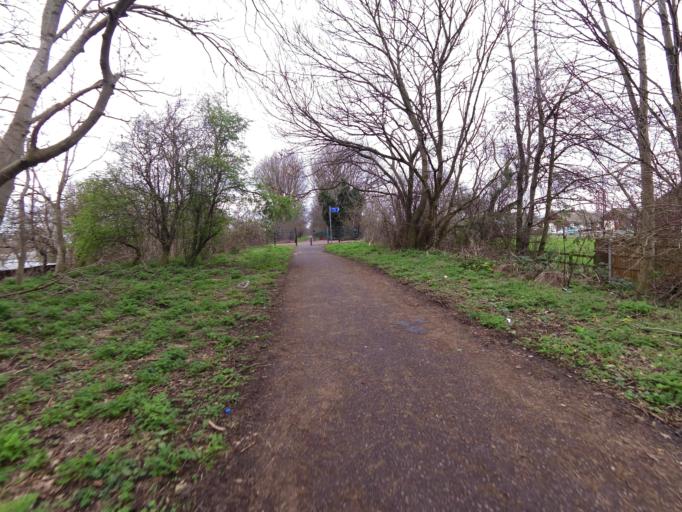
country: GB
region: England
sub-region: Doncaster
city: Bentley
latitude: 53.5427
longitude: -1.1574
